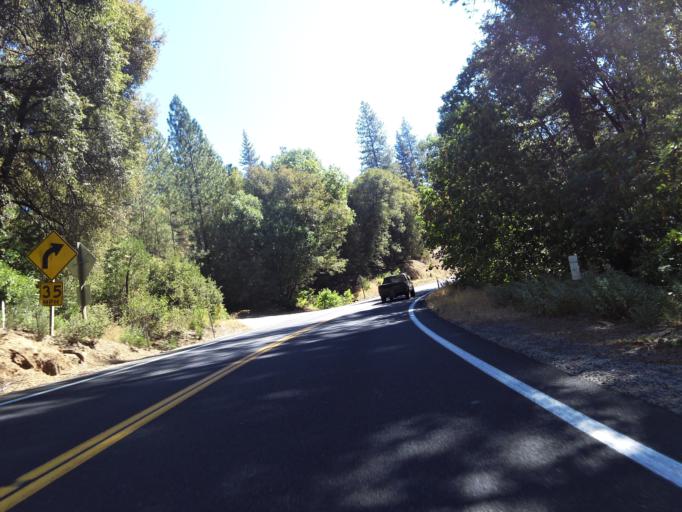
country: US
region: California
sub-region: Calaveras County
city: Forest Meadows
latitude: 38.1652
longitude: -120.4312
